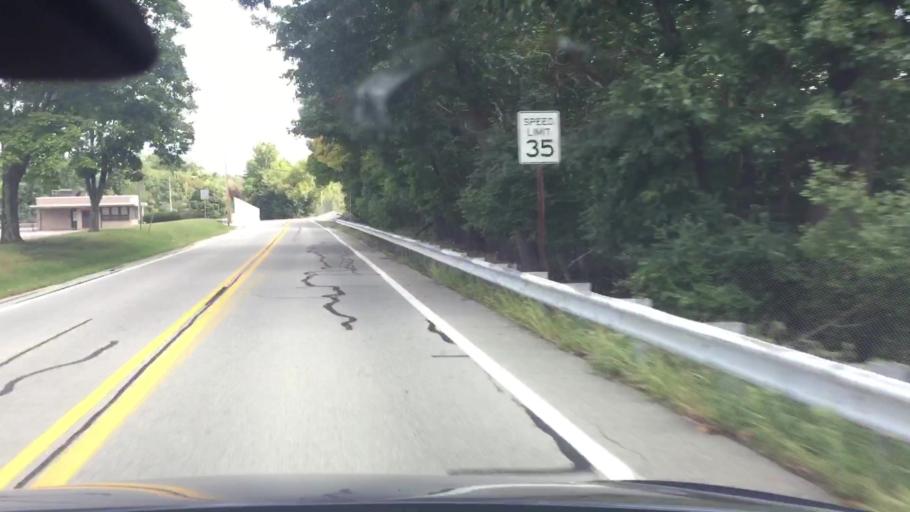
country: US
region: Pennsylvania
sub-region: Allegheny County
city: Cheswick
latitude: 40.5436
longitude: -79.8257
